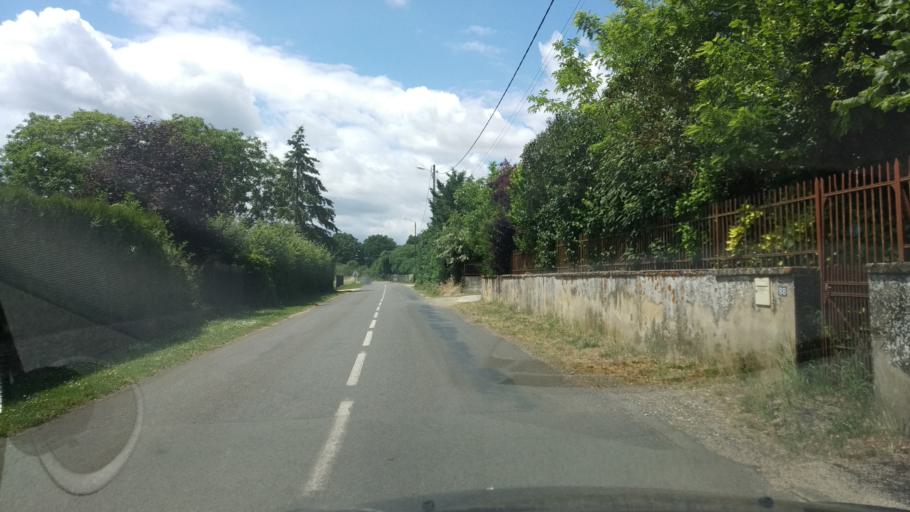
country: FR
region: Poitou-Charentes
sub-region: Departement de la Vienne
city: Vouneuil-sous-Biard
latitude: 46.6065
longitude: 0.2705
